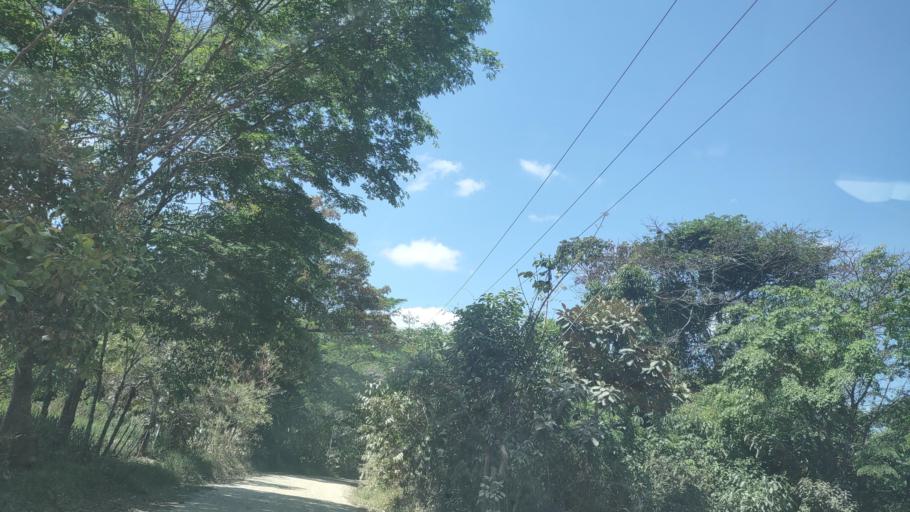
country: MX
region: Veracruz
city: Las Choapas
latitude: 17.7731
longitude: -94.1491
